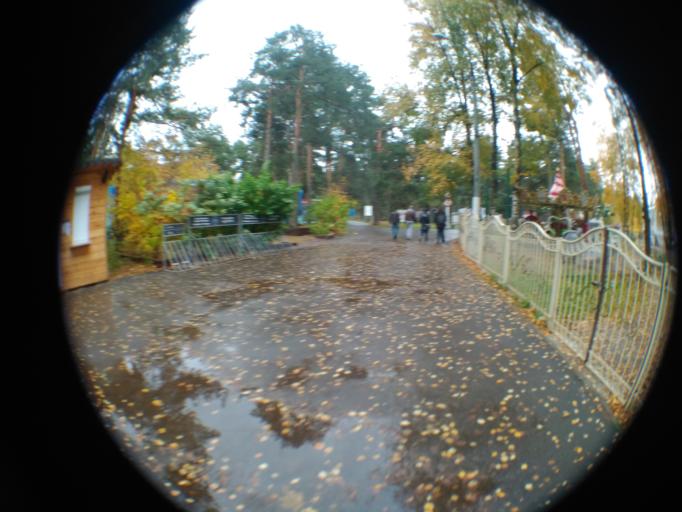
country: RU
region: Moskovskaya
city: Zhukovskiy
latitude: 55.5886
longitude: 38.1263
